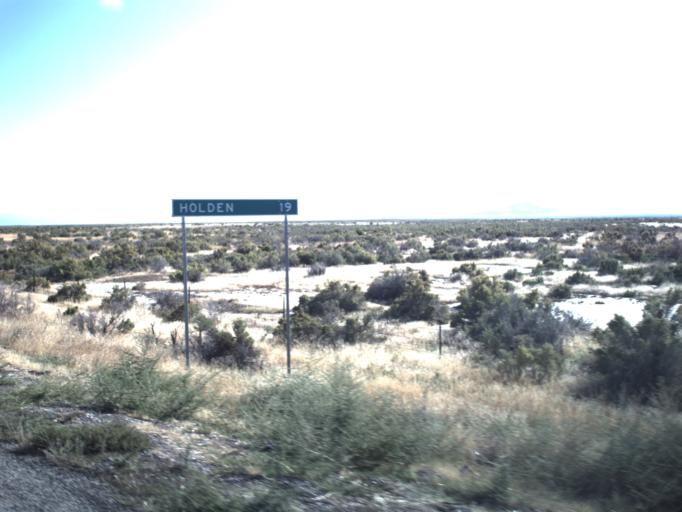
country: US
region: Utah
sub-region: Millard County
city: Delta
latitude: 39.2868
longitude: -112.4638
